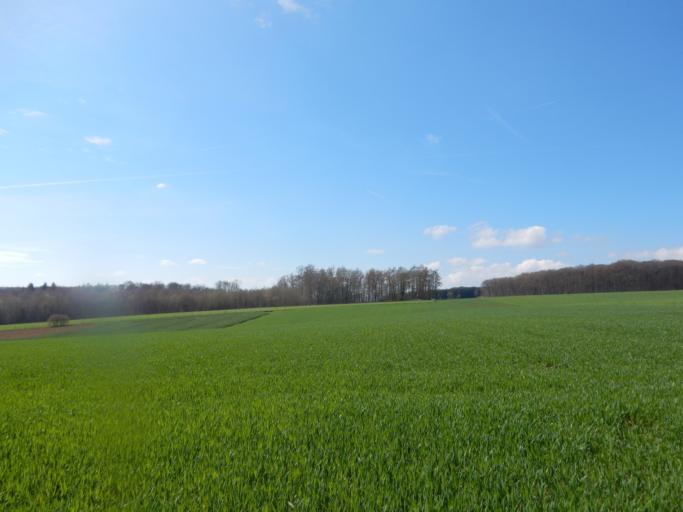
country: LU
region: Diekirch
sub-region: Canton de Diekirch
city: Reisdorf
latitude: 49.8795
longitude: 6.2554
